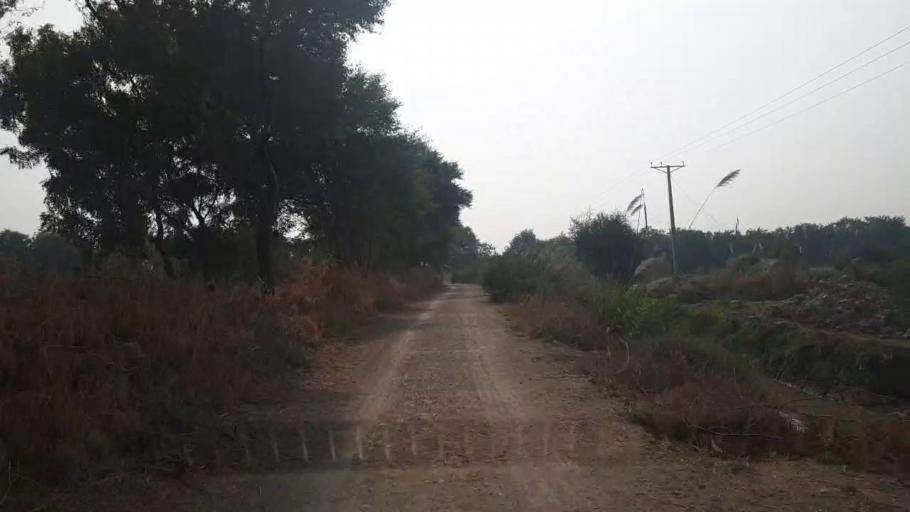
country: PK
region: Sindh
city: Tando Muhammad Khan
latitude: 25.2672
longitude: 68.5099
